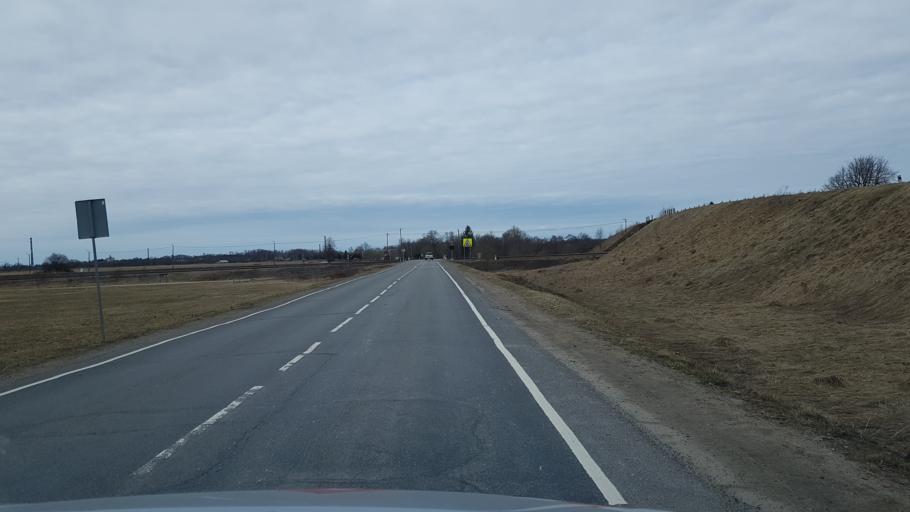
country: EE
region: Ida-Virumaa
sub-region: Sillamaee linn
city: Sillamae
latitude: 59.3721
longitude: 27.7607
